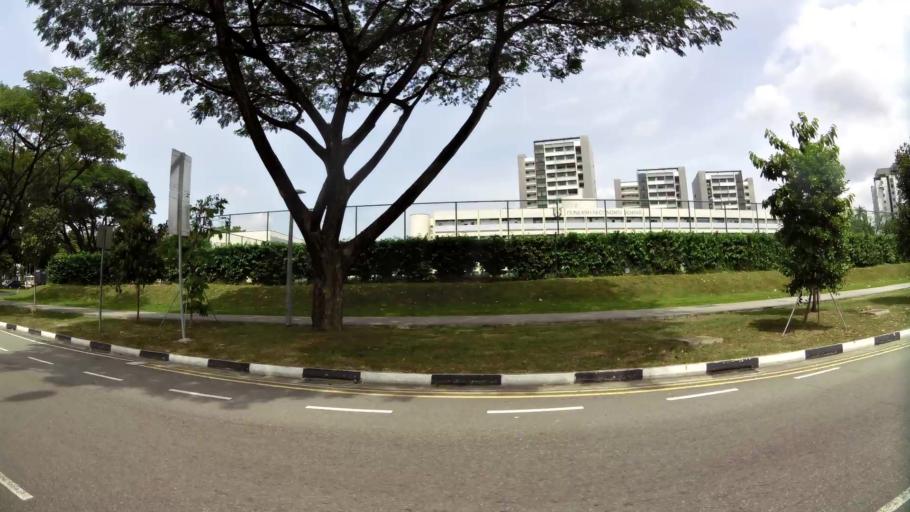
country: MY
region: Johor
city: Johor Bahru
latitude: 1.3409
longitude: 103.7103
